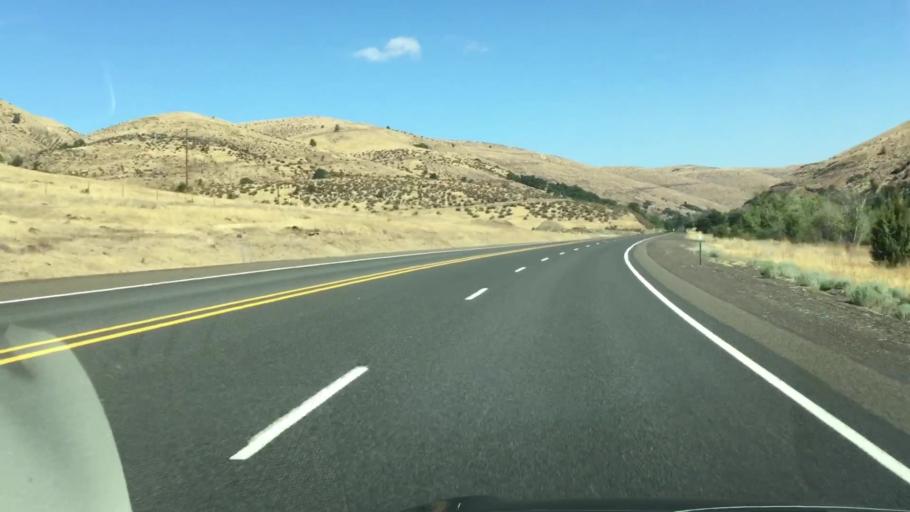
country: US
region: Oregon
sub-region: Wasco County
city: The Dalles
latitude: 45.2622
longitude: -121.1910
